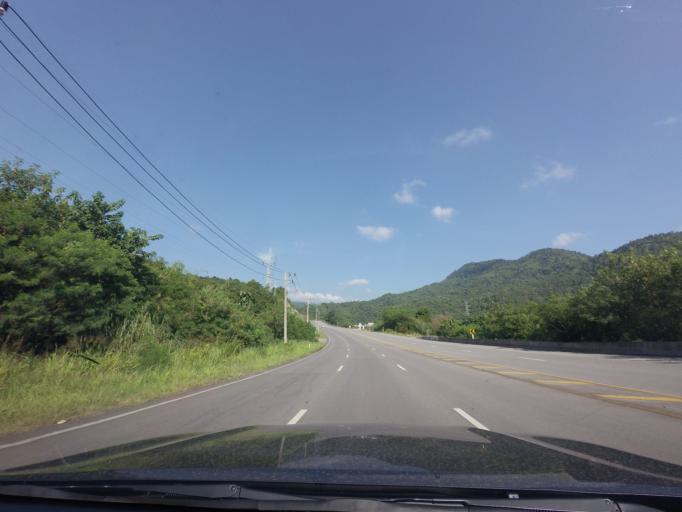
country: TH
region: Phetchabun
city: Lom Sak
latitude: 16.7703
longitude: 101.1359
